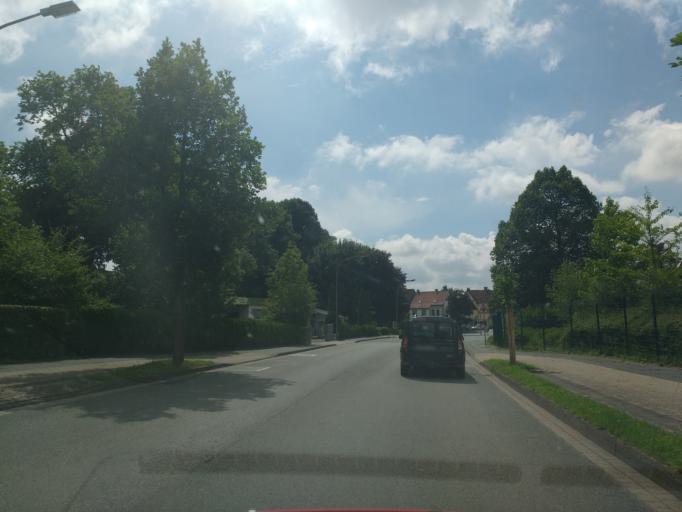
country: DE
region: North Rhine-Westphalia
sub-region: Regierungsbezirk Detmold
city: Blomberg
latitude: 51.9438
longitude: 9.0986
